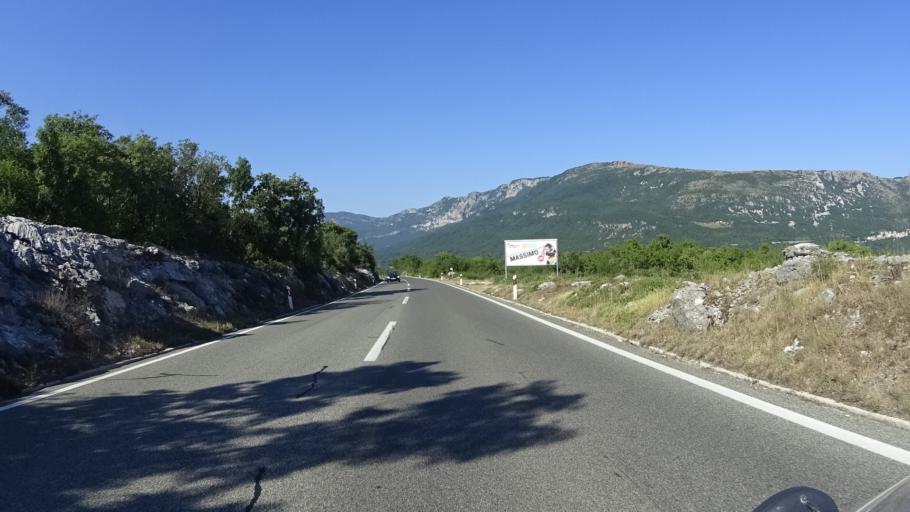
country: HR
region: Istarska
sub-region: Grad Labin
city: Labin
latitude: 45.1375
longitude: 14.1446
